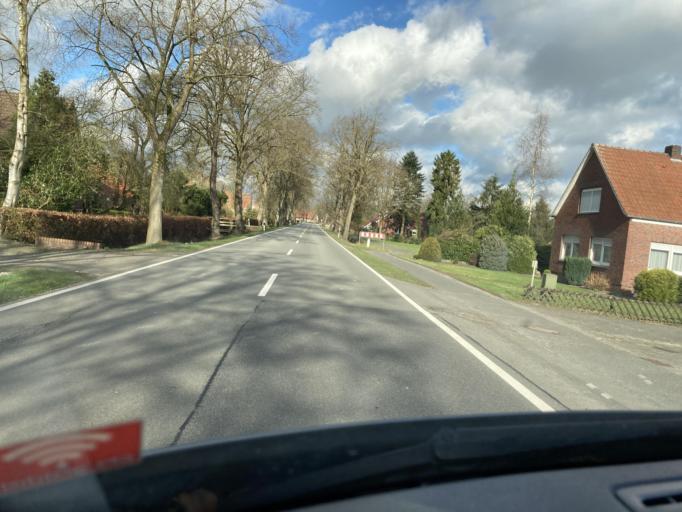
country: DE
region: Lower Saxony
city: Friedeburg
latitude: 53.3590
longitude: 7.8143
